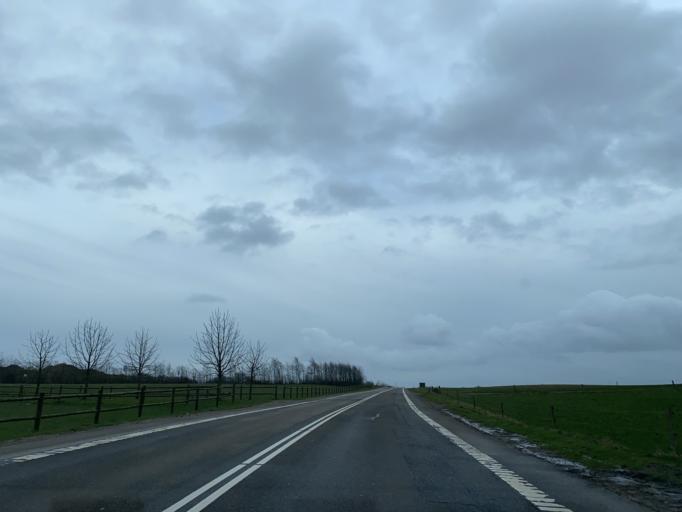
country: DK
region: Central Jutland
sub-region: Viborg Kommune
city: Bjerringbro
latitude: 56.2974
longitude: 9.6003
